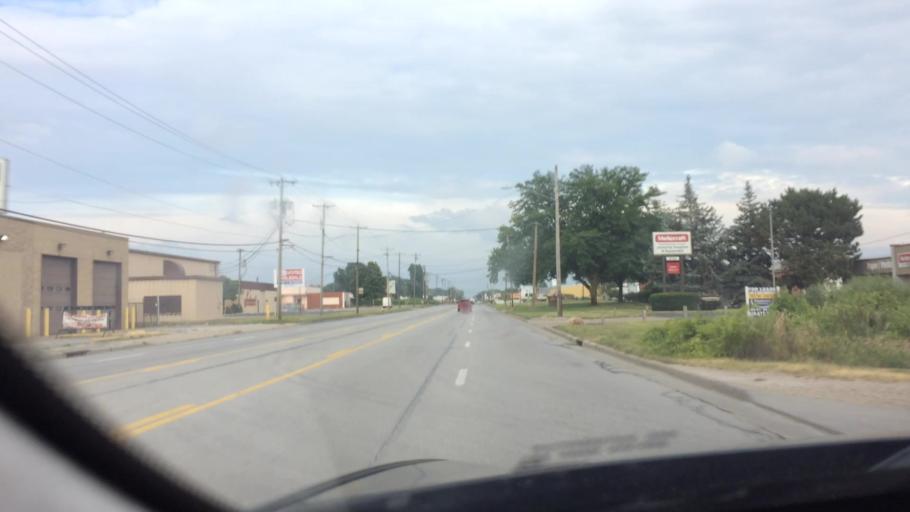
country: US
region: Ohio
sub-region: Lucas County
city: Ottawa Hills
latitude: 41.6380
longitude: -83.6187
